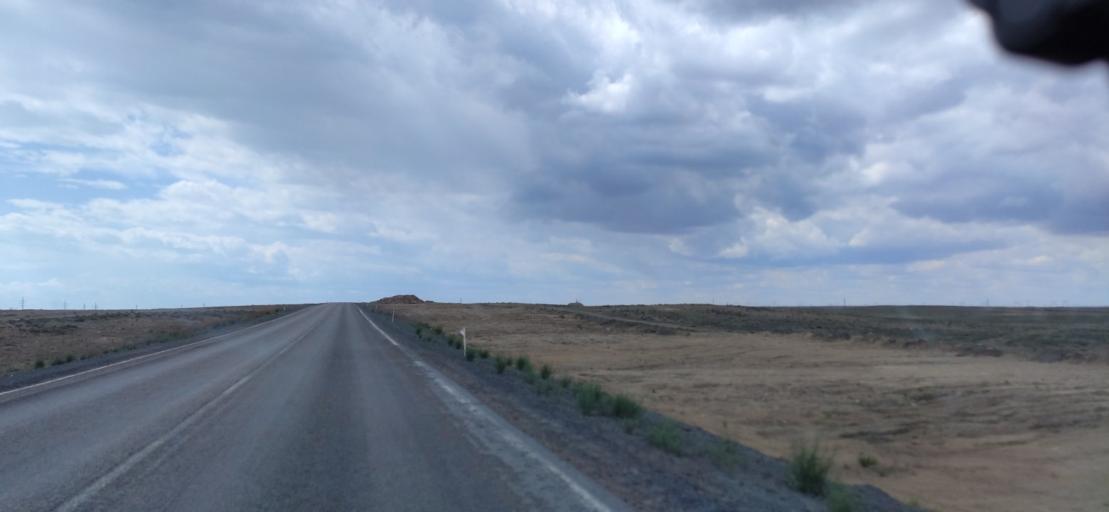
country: KZ
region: Qaraghandy
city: Saryshaghan
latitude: 46.0769
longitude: 73.6035
